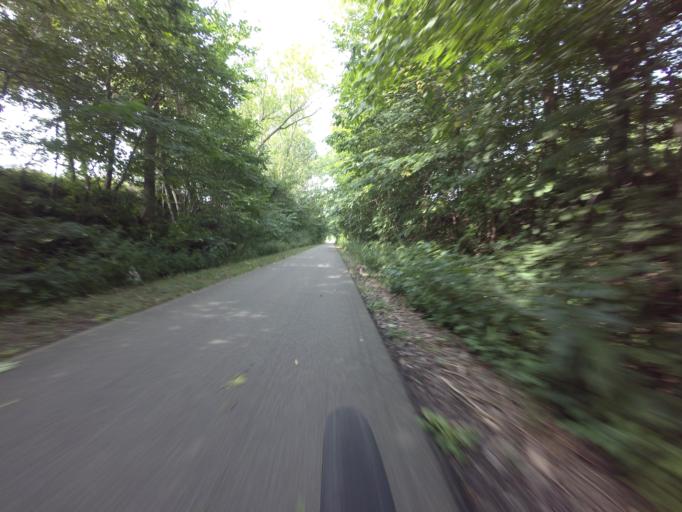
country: DK
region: Zealand
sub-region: Naestved Kommune
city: Naestved
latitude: 55.2512
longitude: 11.7406
